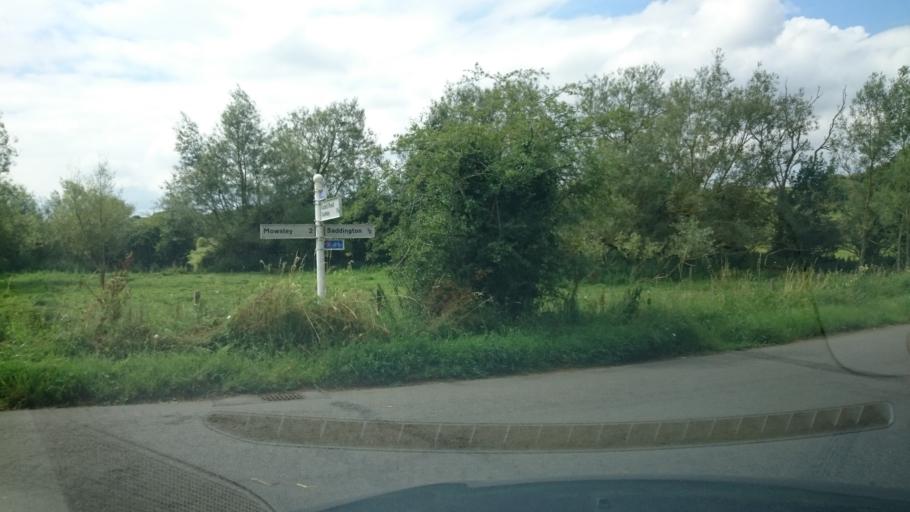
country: GB
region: England
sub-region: Leicestershire
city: Kibworth Harcourt
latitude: 52.5151
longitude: -1.0282
